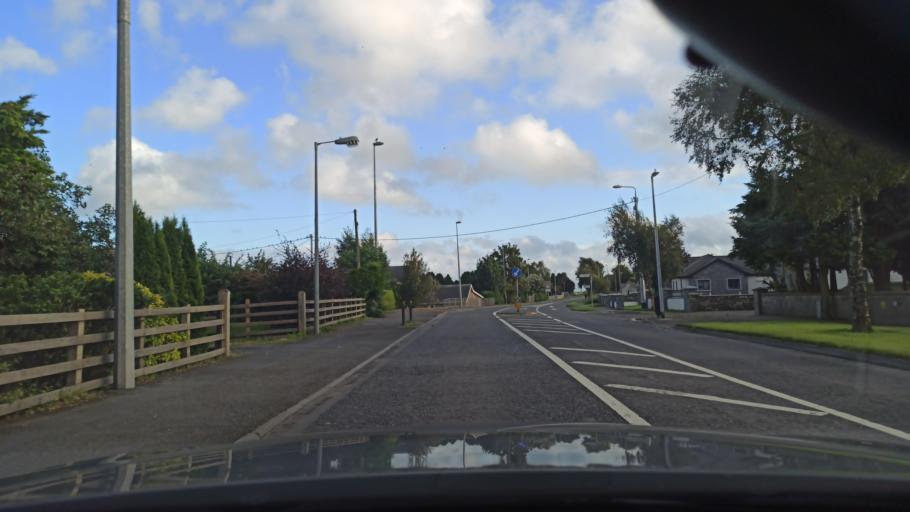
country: IE
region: Munster
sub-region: North Tipperary
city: Roscrea
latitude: 52.9396
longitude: -7.7880
